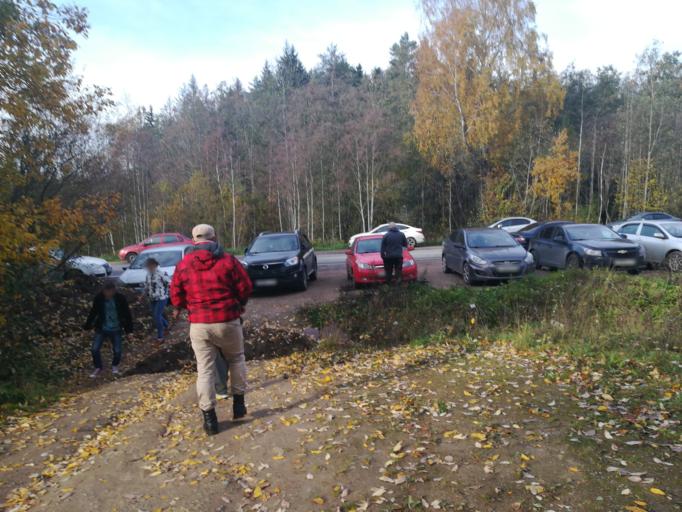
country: RU
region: Leningrad
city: Sista-Palkino
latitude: 59.5925
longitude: 28.8284
